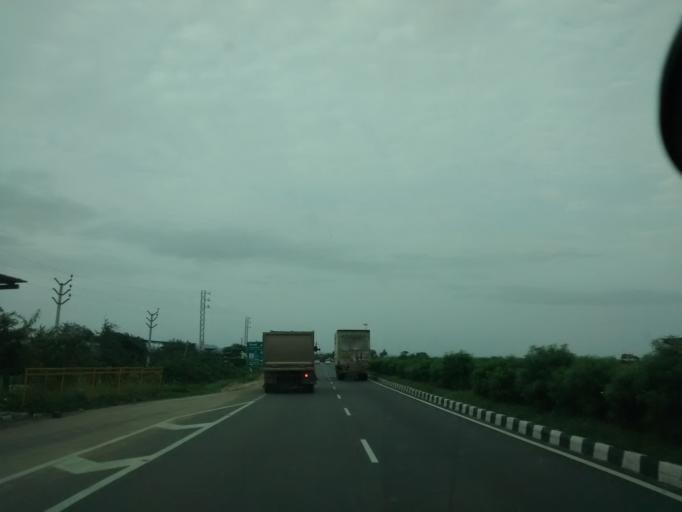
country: IN
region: Telangana
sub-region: Mahbubnagar
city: Wanparti
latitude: 16.3872
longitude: 77.9367
